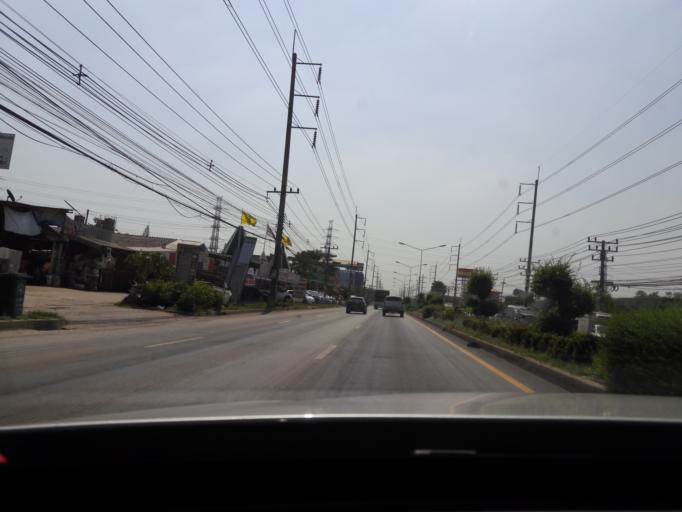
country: TH
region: Samut Sakhon
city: Krathum Baen
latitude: 13.6074
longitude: 100.2867
